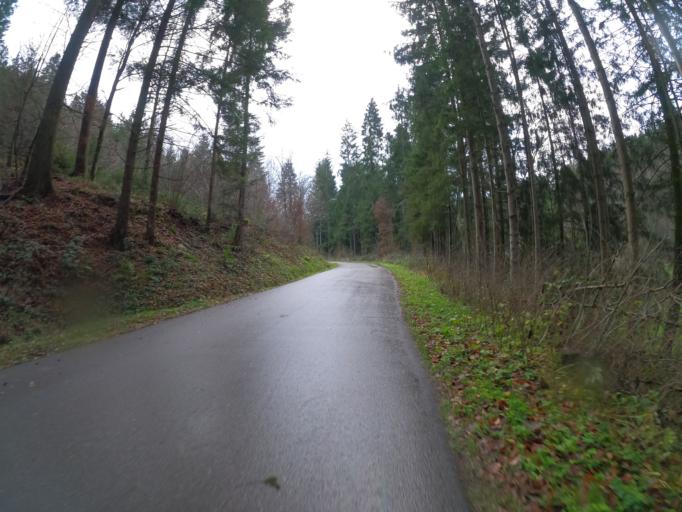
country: DE
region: Baden-Wuerttemberg
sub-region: Regierungsbezirk Stuttgart
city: Lorch
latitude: 48.7798
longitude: 9.7205
